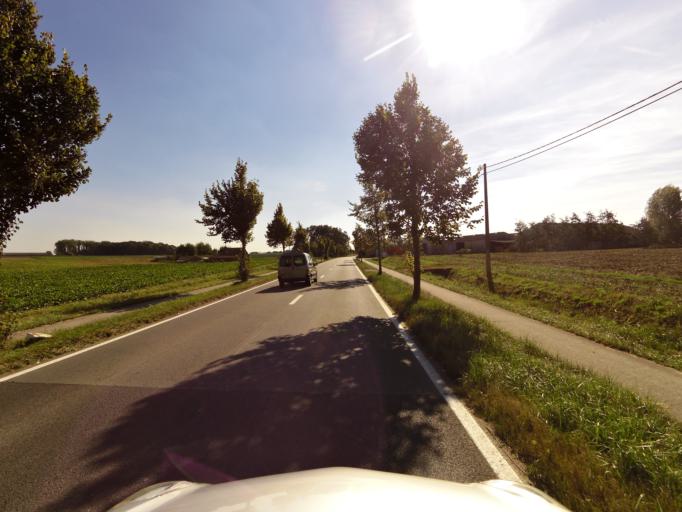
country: BE
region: Flanders
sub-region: Provincie West-Vlaanderen
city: Poperinge
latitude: 50.8872
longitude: 2.7392
